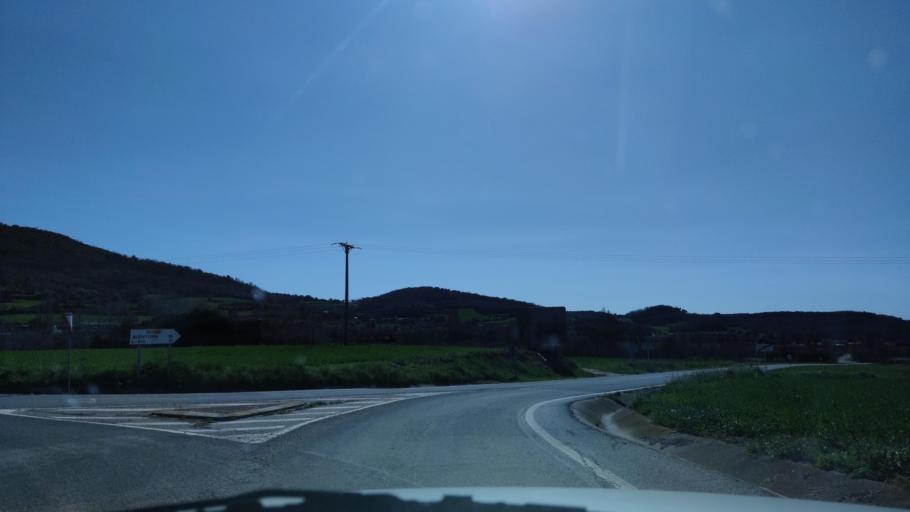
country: ES
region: Catalonia
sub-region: Provincia de Lleida
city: Artesa de Segre
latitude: 41.9896
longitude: 1.0233
